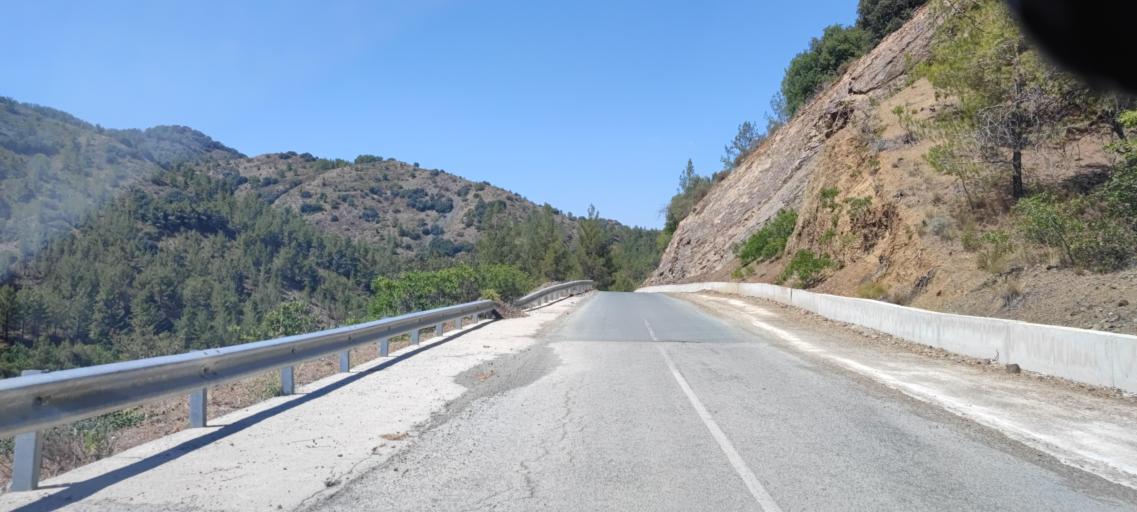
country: CY
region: Lefkosia
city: Kakopetria
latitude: 34.9260
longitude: 32.8020
